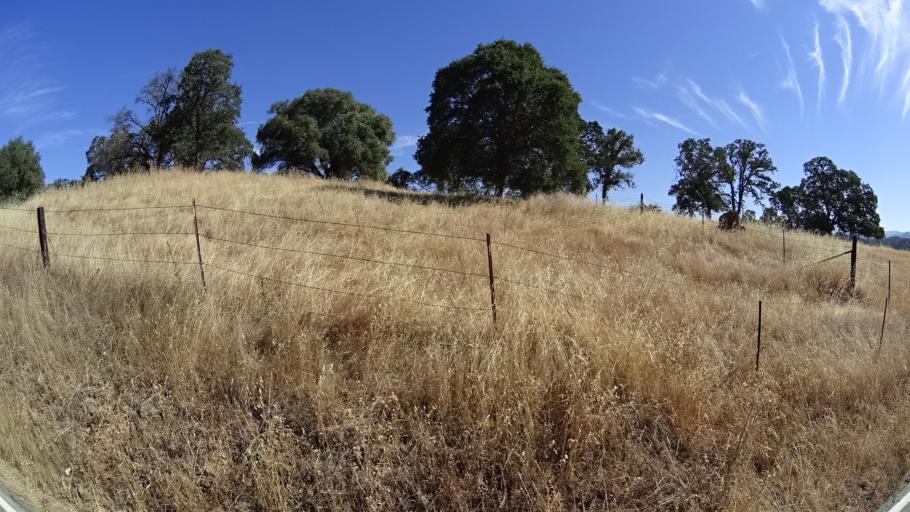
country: US
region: California
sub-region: Calaveras County
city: San Andreas
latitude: 38.1490
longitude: -120.6096
